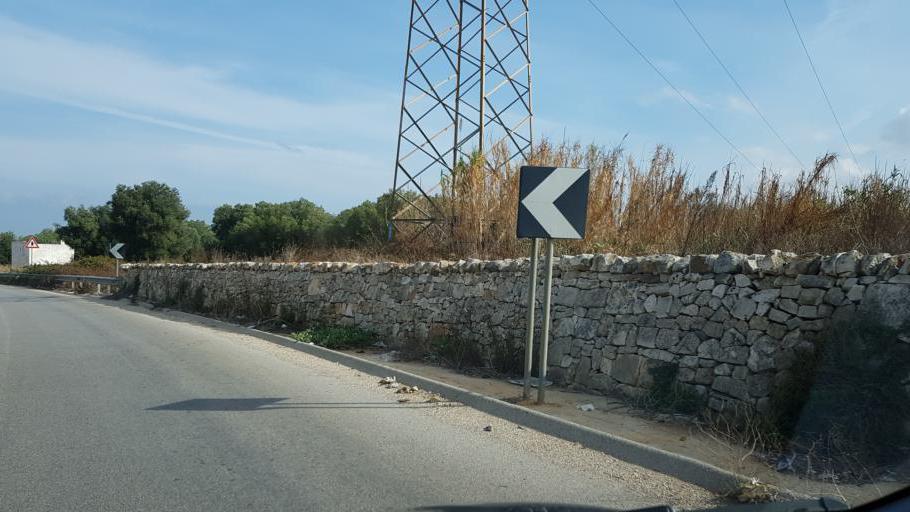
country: IT
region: Apulia
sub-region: Provincia di Brindisi
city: Ostuni
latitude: 40.7449
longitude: 17.5813
